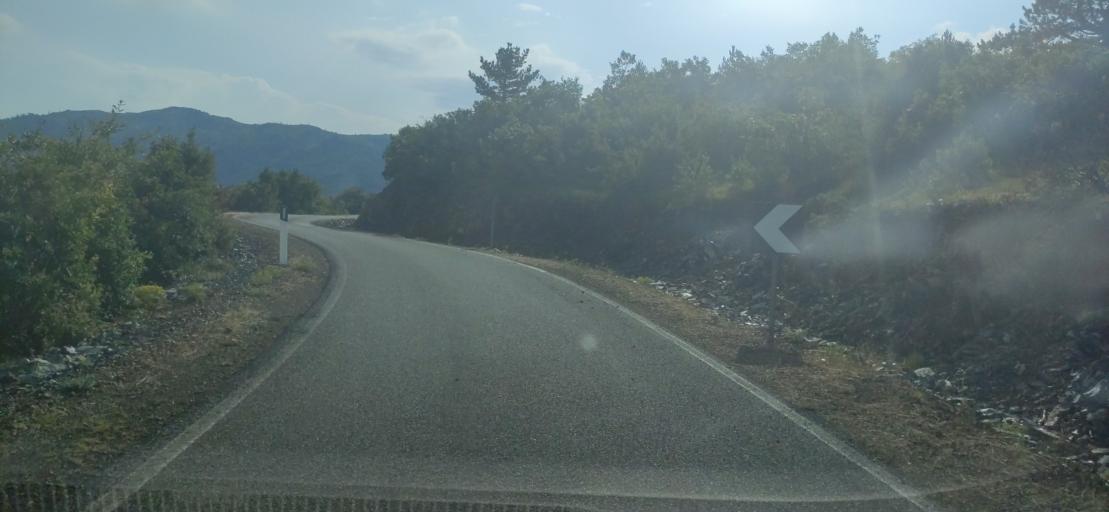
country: AL
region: Shkoder
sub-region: Rrethi i Pukes
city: Iballe
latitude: 42.1732
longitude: 19.9946
